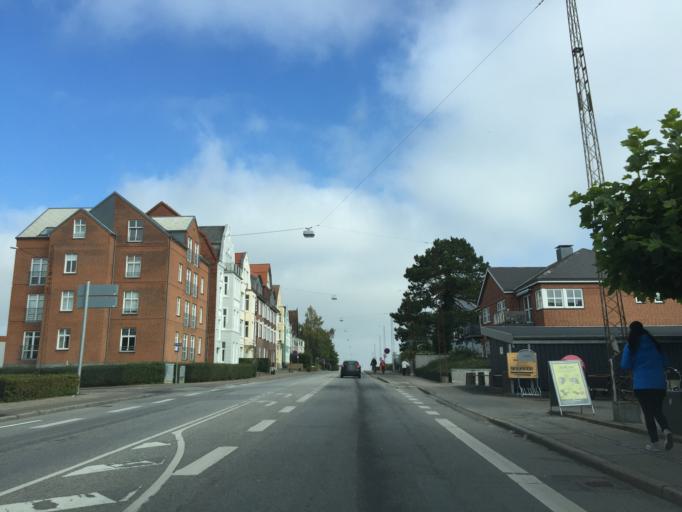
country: DK
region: South Denmark
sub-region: Sonderborg Kommune
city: Sonderborg
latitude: 54.9142
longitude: 9.7971
